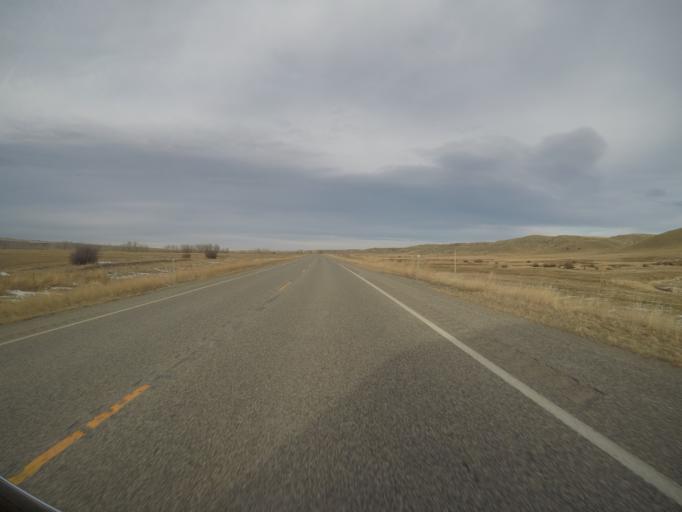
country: US
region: Montana
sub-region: Stillwater County
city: Absarokee
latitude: 45.4446
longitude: -109.4479
